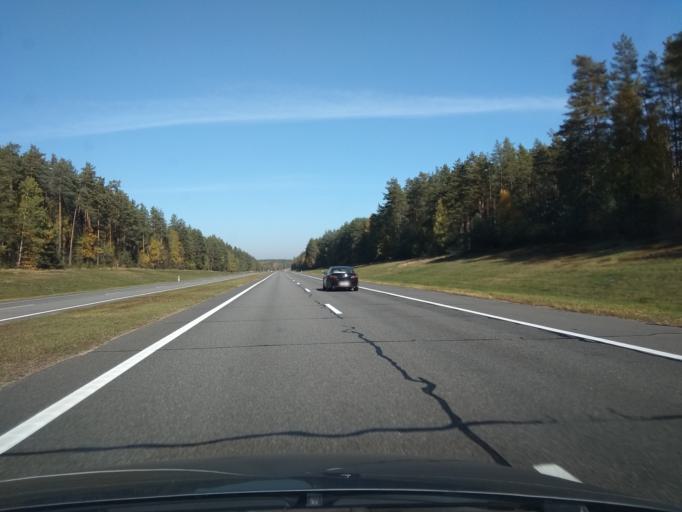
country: BY
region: Brest
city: Baranovichi
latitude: 53.0110
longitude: 25.7774
